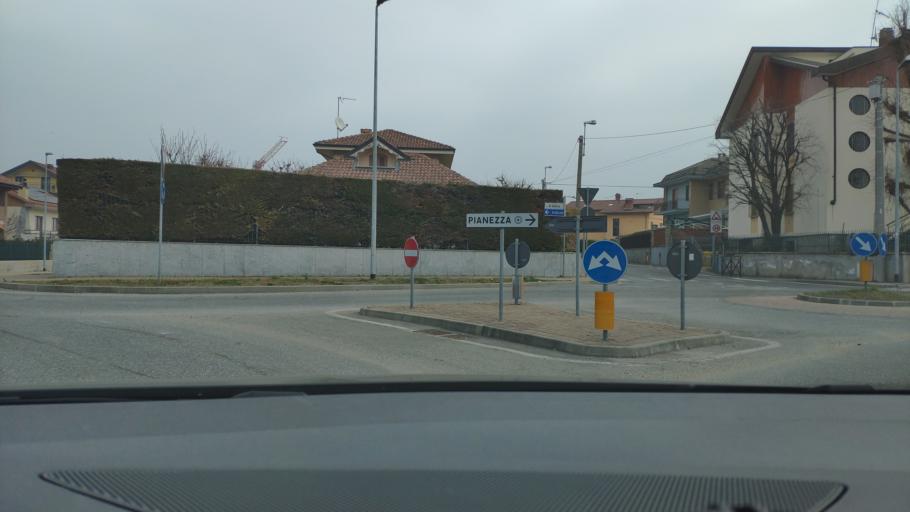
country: IT
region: Piedmont
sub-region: Provincia di Torino
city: Pianezza
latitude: 45.1145
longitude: 7.5443
